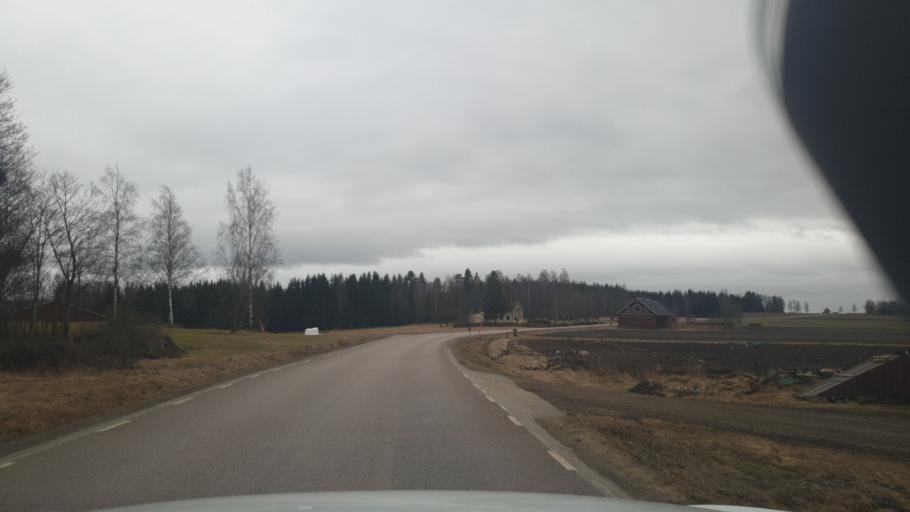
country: SE
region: Vaermland
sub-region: Eda Kommun
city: Charlottenberg
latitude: 59.7681
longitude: 12.1613
